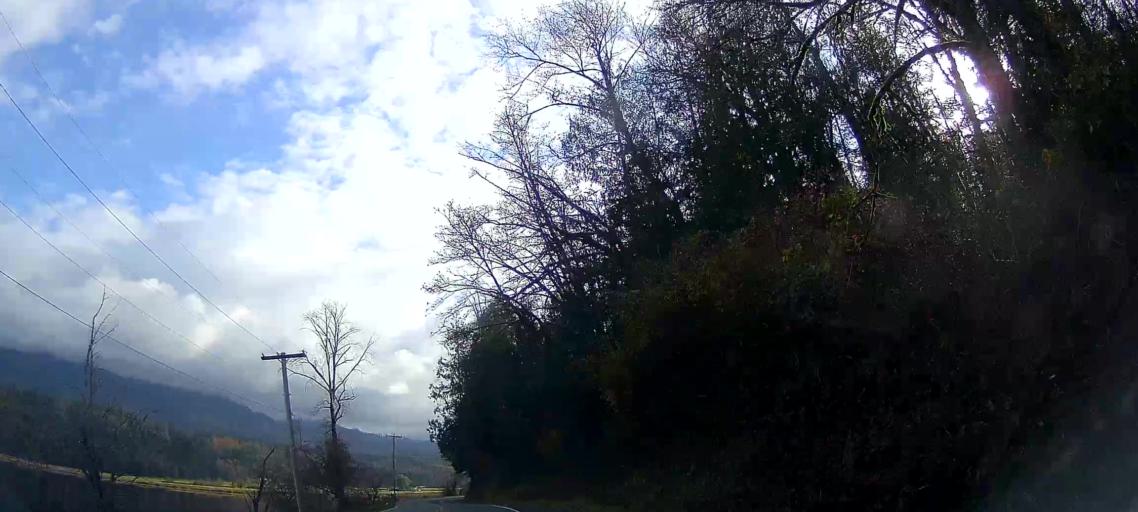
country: US
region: Washington
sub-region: Skagit County
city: Clear Lake
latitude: 48.4479
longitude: -122.2233
